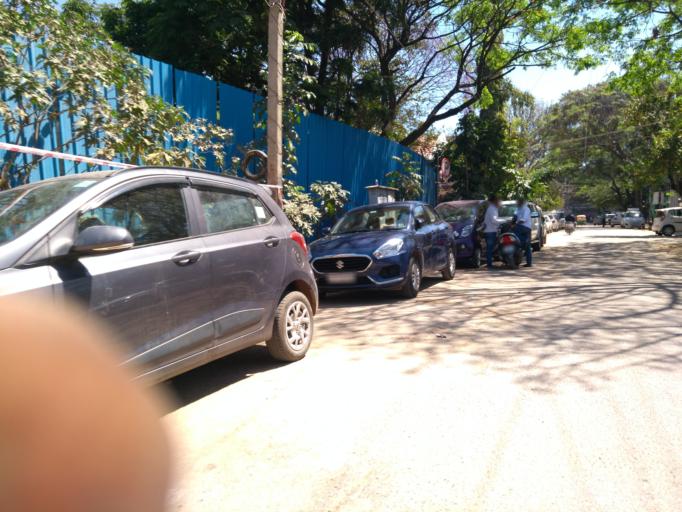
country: IN
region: Karnataka
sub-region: Bangalore Urban
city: Bangalore
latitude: 12.9691
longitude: 77.6529
